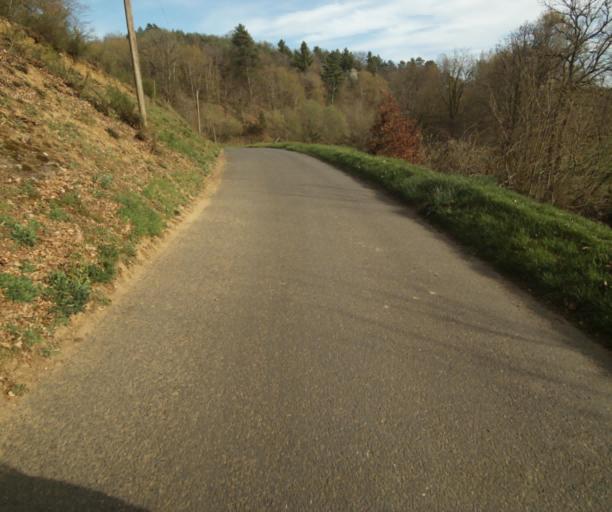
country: FR
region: Limousin
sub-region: Departement de la Correze
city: Naves
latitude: 45.2953
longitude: 1.7569
